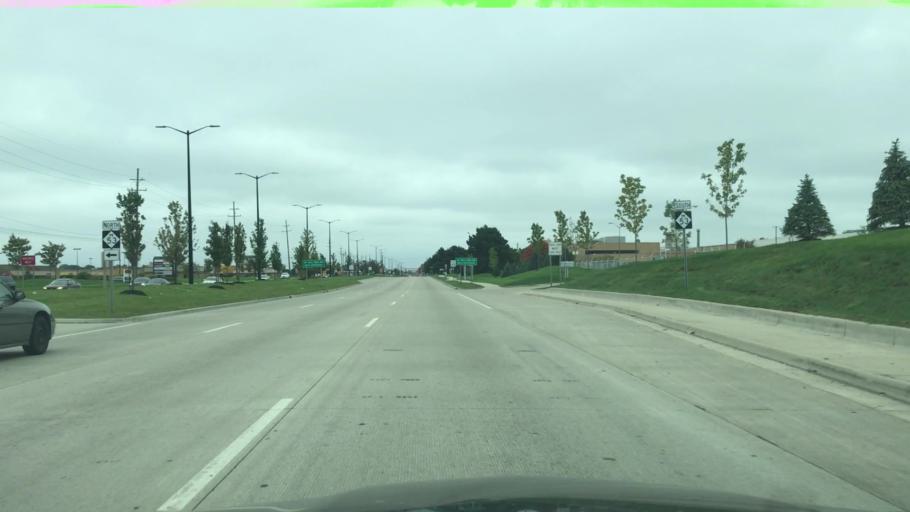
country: US
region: Michigan
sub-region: Macomb County
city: Sterling Heights
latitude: 42.5736
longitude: -83.0303
